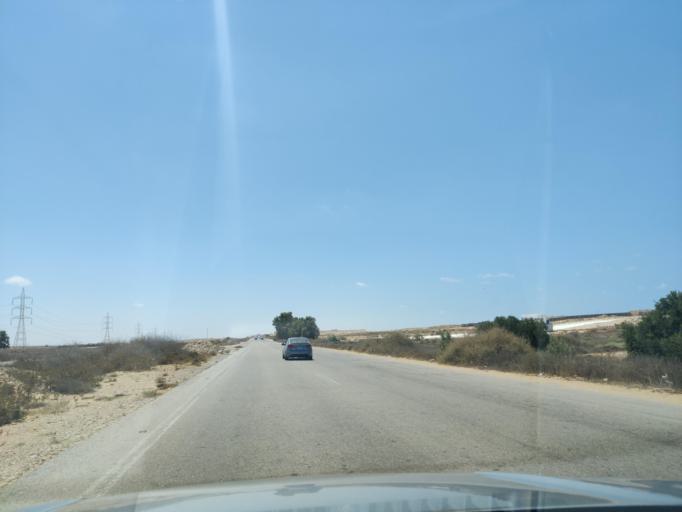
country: EG
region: Muhafazat Matruh
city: Al `Alamayn
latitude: 31.0671
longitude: 28.1019
